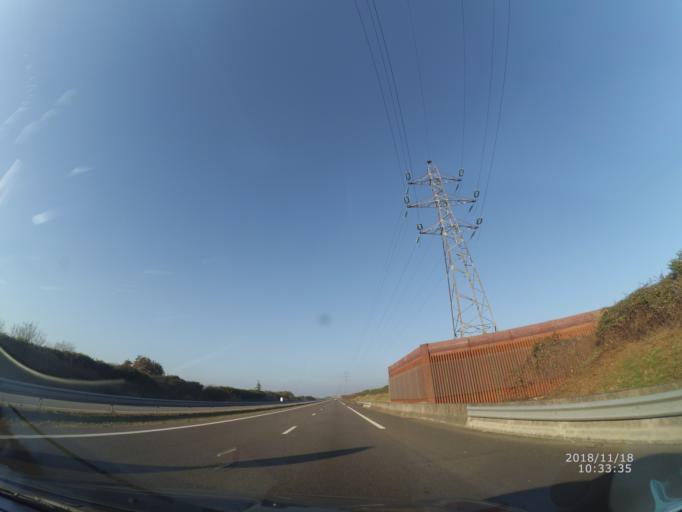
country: FR
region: Pays de la Loire
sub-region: Departement de la Loire-Atlantique
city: Saint-Jean-de-Boiseau
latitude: 47.1851
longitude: -1.7331
